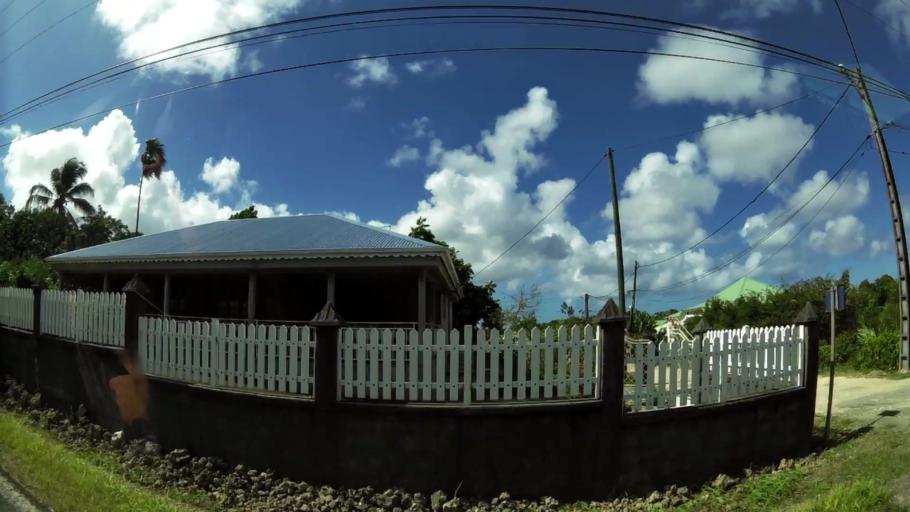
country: GP
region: Guadeloupe
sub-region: Guadeloupe
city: Anse-Bertrand
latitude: 16.4527
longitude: -61.4784
